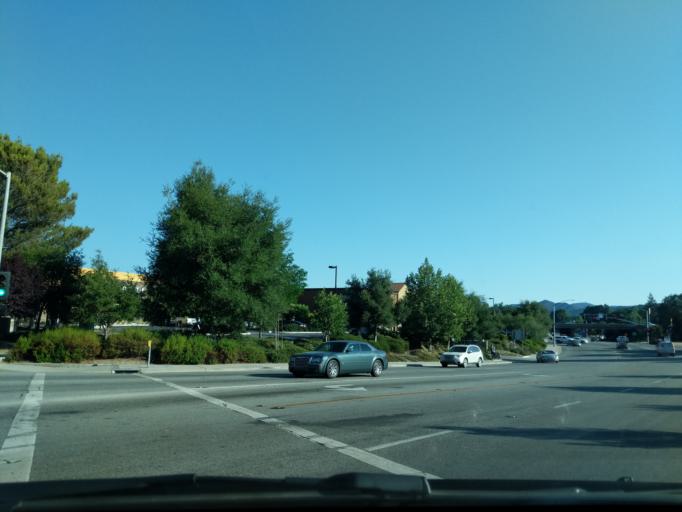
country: US
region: California
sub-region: San Luis Obispo County
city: Atascadero
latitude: 35.4875
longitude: -120.6641
